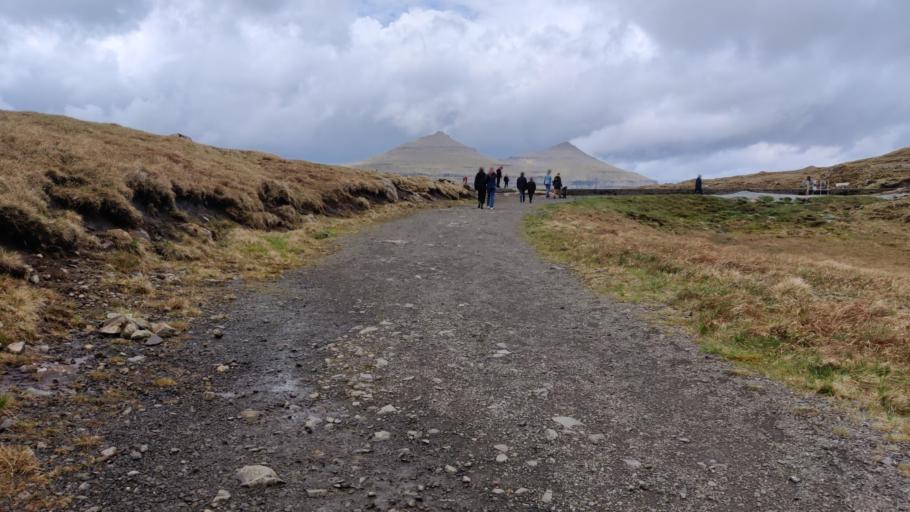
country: FO
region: Nordoyar
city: Klaksvik
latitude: 62.2266
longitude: -6.6099
